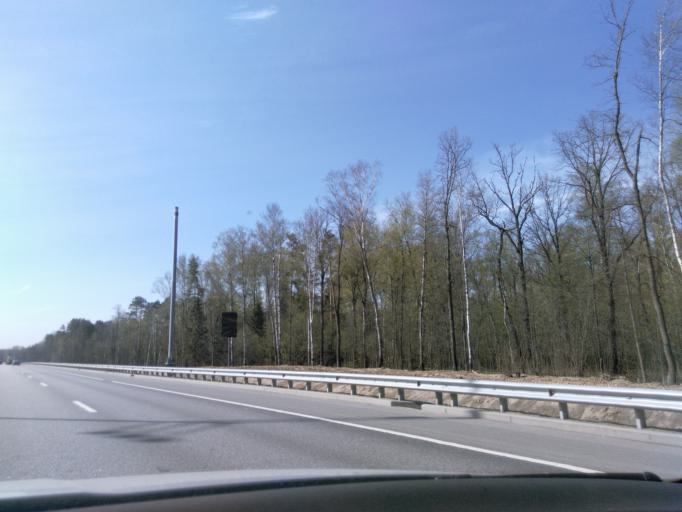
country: RU
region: Moscow
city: Khimki
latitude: 55.9271
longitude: 37.4535
